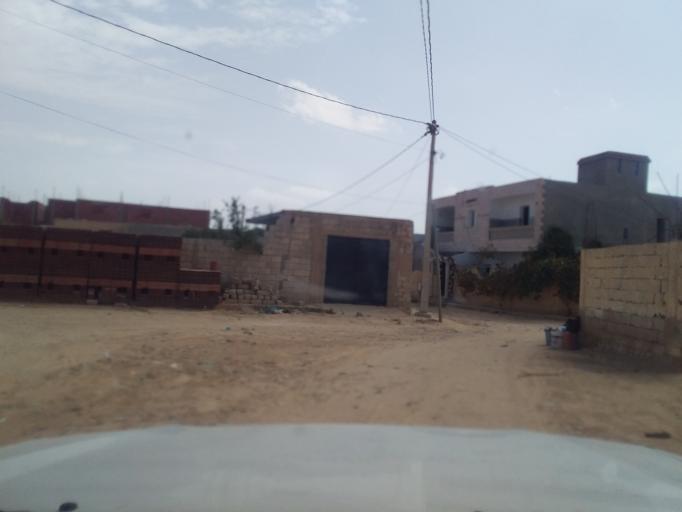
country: TN
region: Qabis
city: Matmata
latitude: 33.6155
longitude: 10.2758
